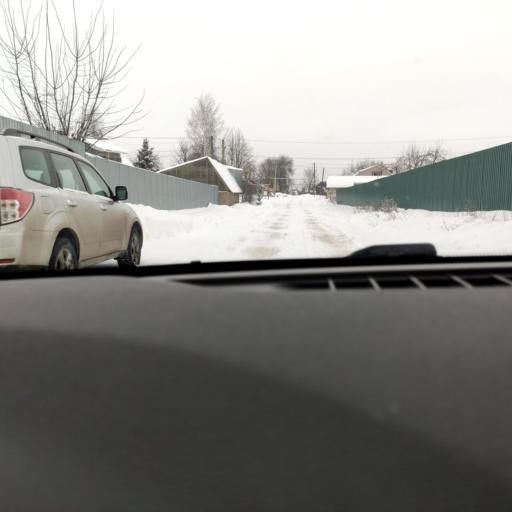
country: RU
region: Samara
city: Smyshlyayevka
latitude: 53.2409
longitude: 50.3476
